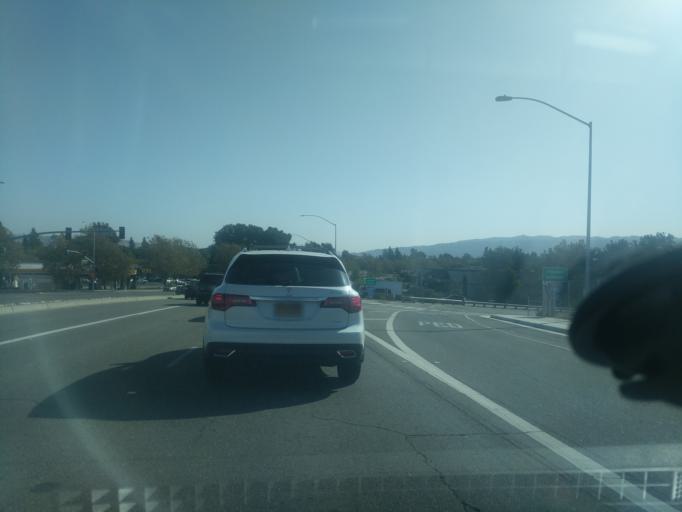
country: US
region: California
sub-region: Alameda County
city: Pleasanton
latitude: 37.7010
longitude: -121.8721
